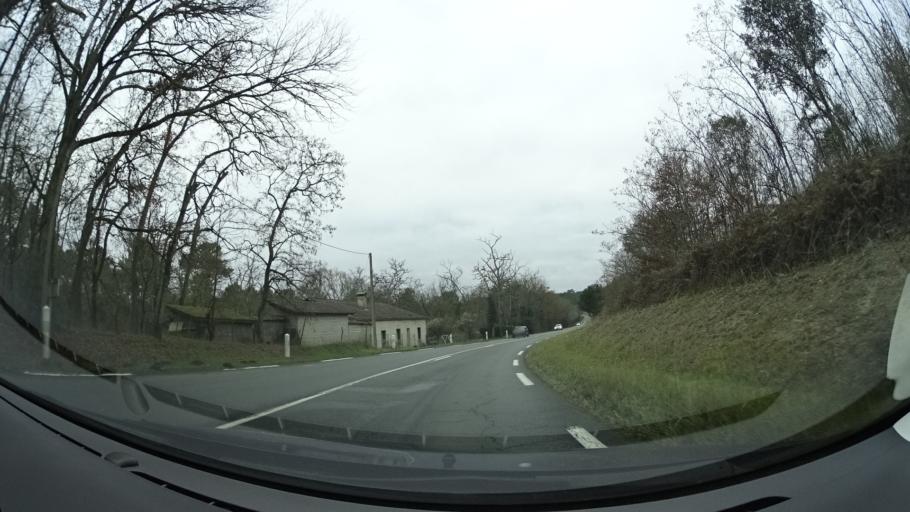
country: FR
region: Aquitaine
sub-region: Departement du Lot-et-Garonne
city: Buzet-sur-Baise
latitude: 44.2344
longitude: 0.2323
